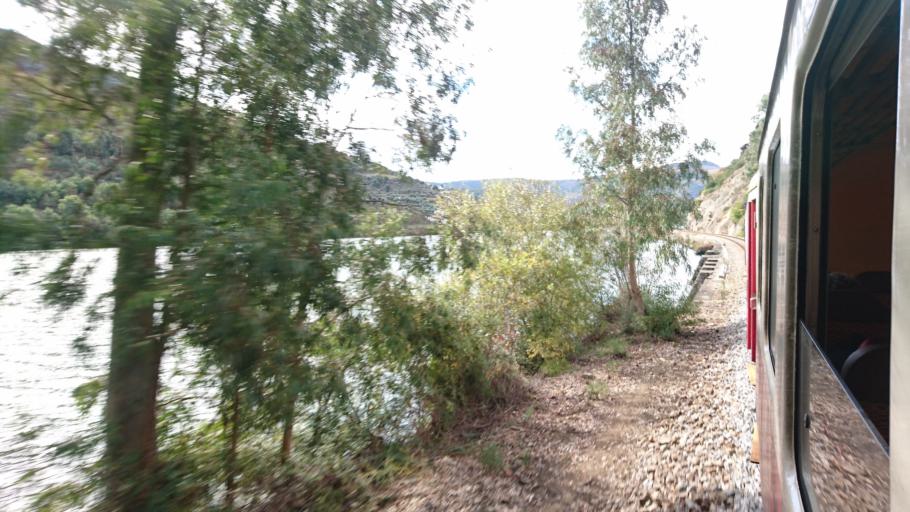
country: PT
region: Viseu
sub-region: Armamar
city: Armamar
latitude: 41.1609
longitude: -7.6702
